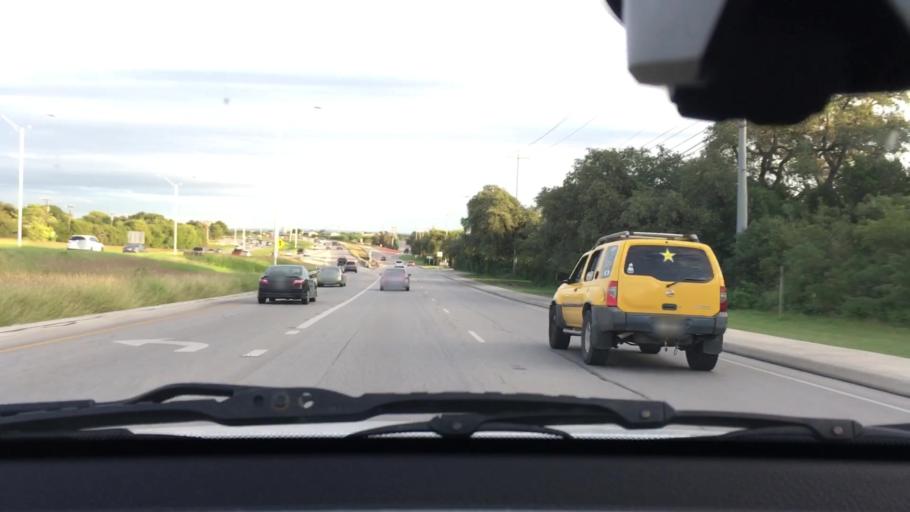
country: US
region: Texas
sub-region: Bexar County
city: Live Oak
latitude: 29.5531
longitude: -98.3227
